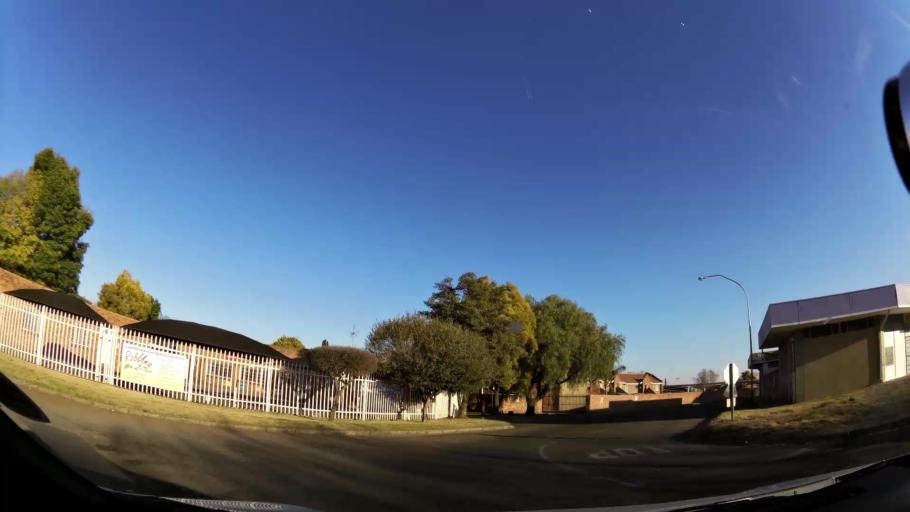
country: ZA
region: Gauteng
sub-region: Ekurhuleni Metropolitan Municipality
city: Germiston
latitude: -26.2869
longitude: 28.1176
